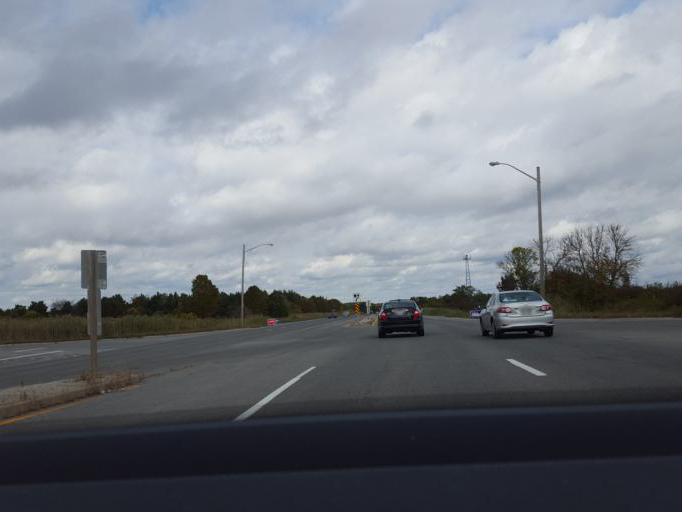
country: CA
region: Ontario
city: Pickering
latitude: 43.8637
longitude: -79.1463
